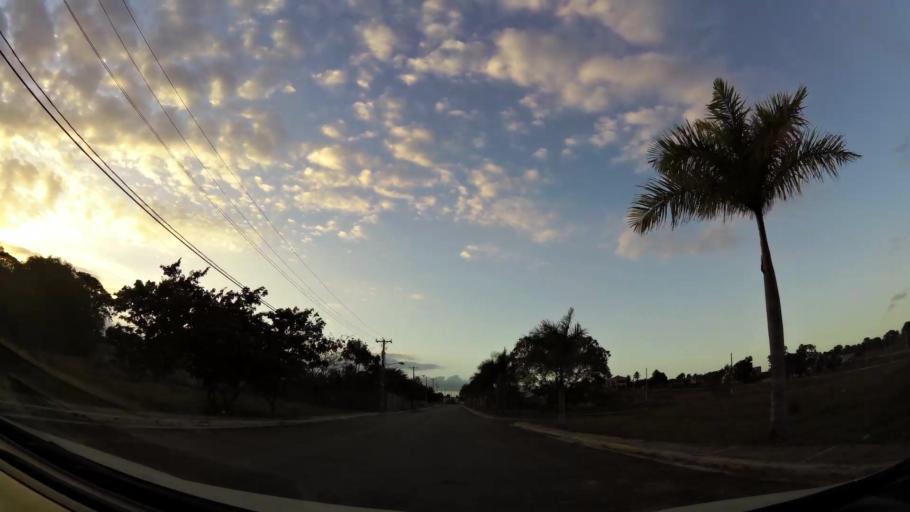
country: DO
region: Nacional
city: La Agustina
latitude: 18.5651
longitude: -69.9379
